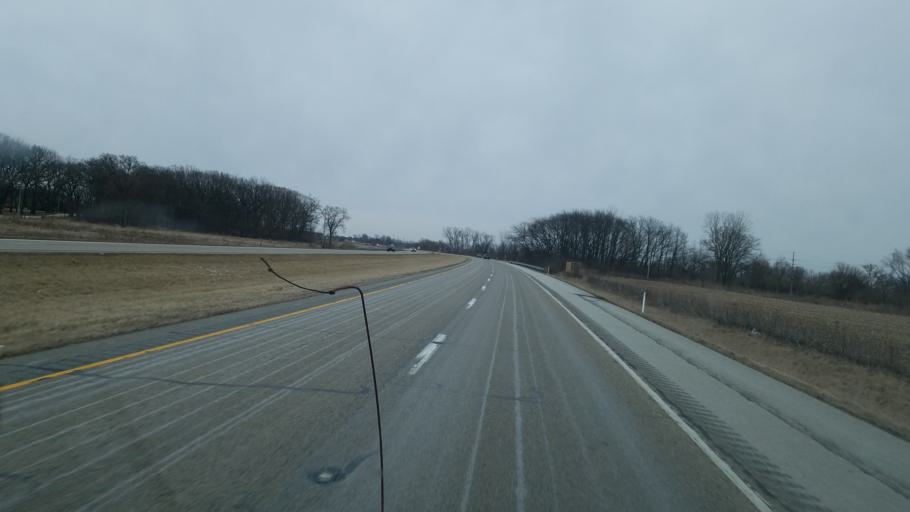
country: US
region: Indiana
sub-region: LaPorte County
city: Kingsford Heights
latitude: 41.4114
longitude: -86.7682
